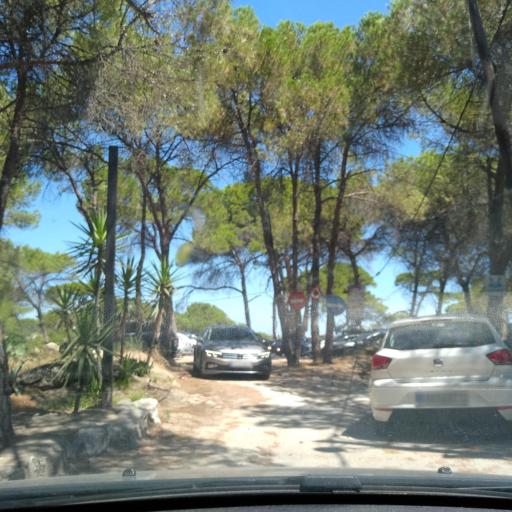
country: GR
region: Central Macedonia
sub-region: Nomos Chalkidikis
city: Neos Marmaras
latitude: 40.1922
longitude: 23.8077
